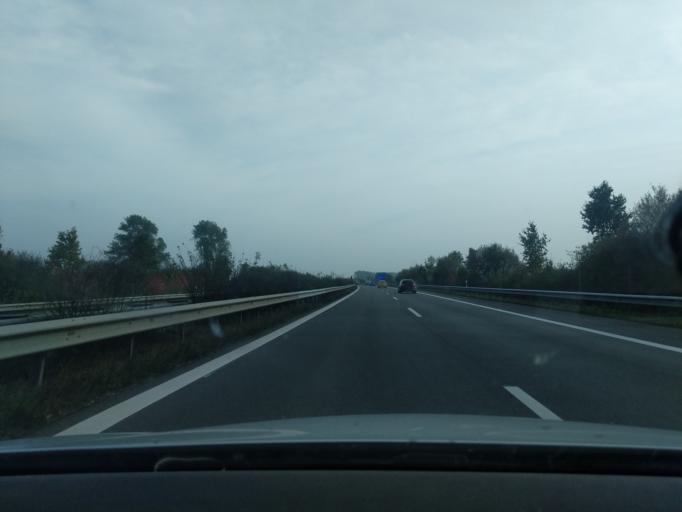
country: DE
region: Lower Saxony
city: Dollern
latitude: 53.5518
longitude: 9.5627
